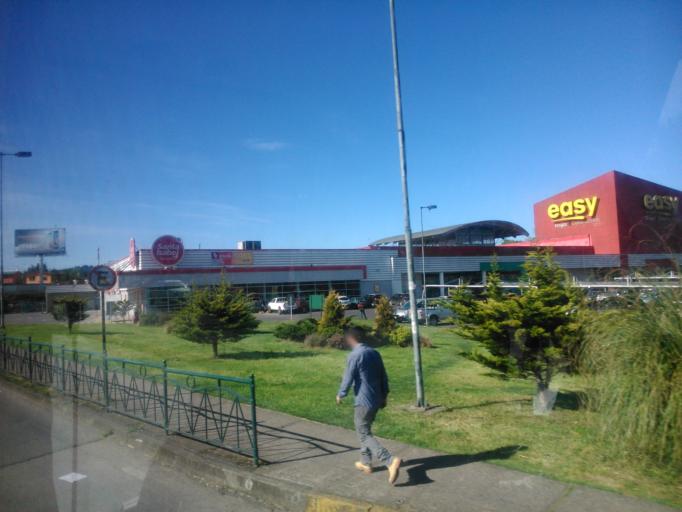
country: CL
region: Araucania
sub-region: Provincia de Cautin
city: Temuco
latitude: -38.7468
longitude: -72.6088
